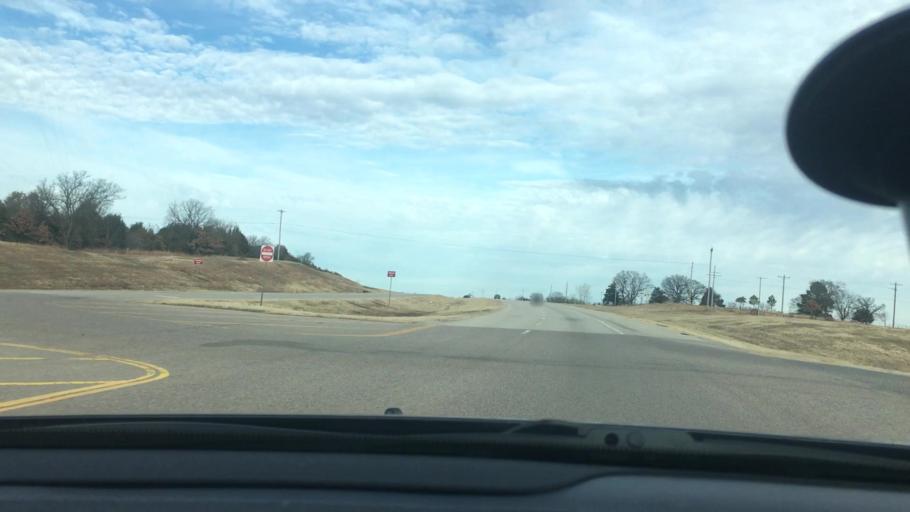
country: US
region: Oklahoma
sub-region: Pontotoc County
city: Byng
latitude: 34.8995
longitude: -96.6748
